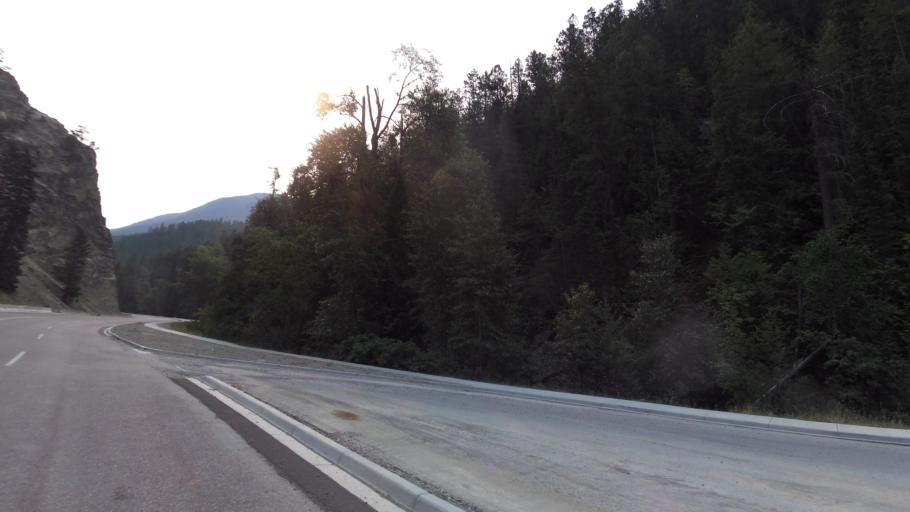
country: CA
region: British Columbia
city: Invermere
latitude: 50.6333
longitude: -116.0519
